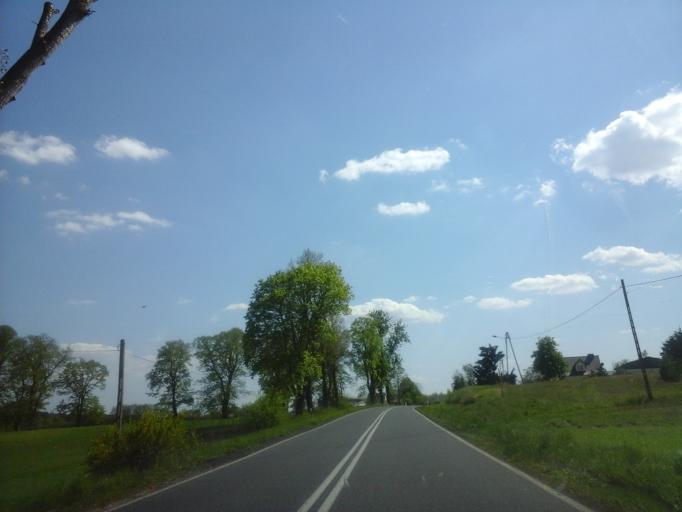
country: PL
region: Lubusz
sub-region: Powiat strzelecko-drezdenecki
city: Dobiegniew
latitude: 52.9885
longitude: 15.7491
